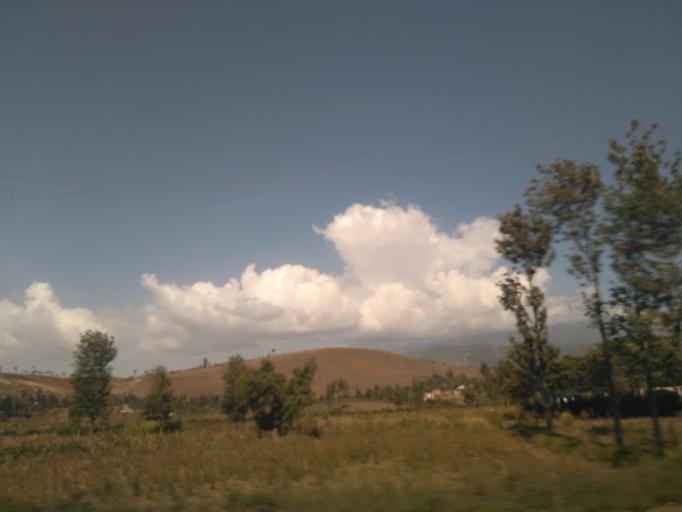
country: TZ
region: Arusha
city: Arusha
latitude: -3.2273
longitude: 36.6070
